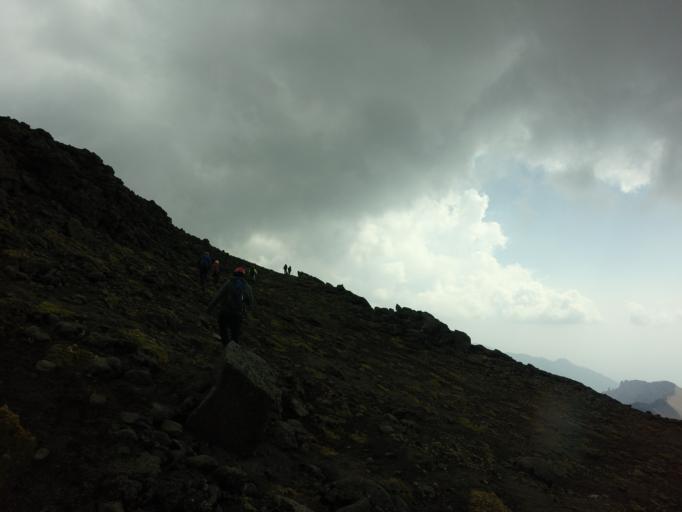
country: MX
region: Mexico
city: Amecameca de Juarez
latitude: 19.1527
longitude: -98.6411
